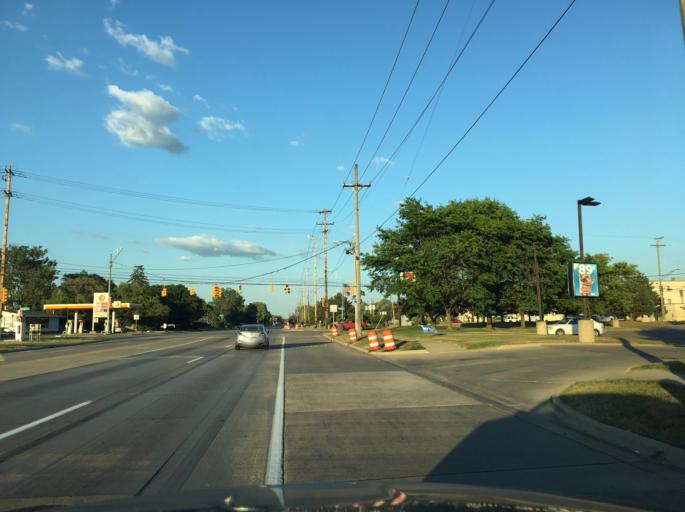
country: US
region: Michigan
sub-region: Macomb County
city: Clinton
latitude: 42.5544
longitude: -82.9113
